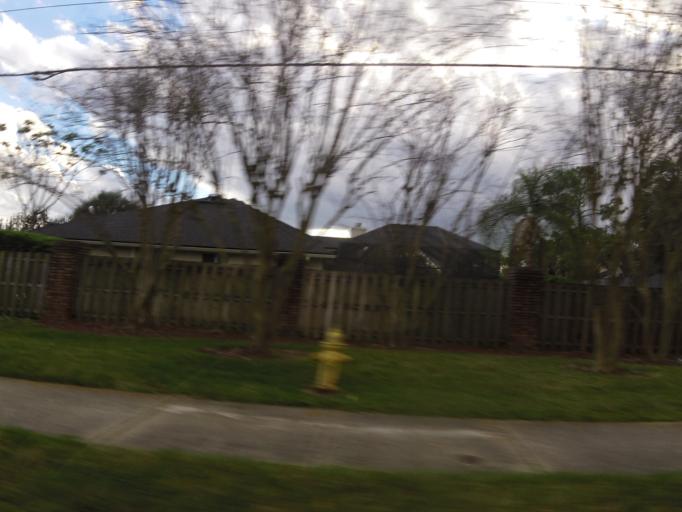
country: US
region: Florida
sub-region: Saint Johns County
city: Fruit Cove
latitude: 30.2175
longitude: -81.5898
